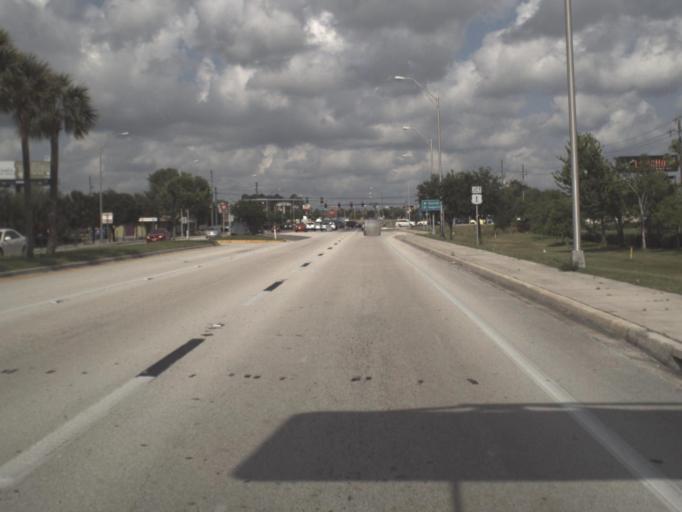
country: US
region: Florida
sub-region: Saint Johns County
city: Saint Augustine South
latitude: 29.8670
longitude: -81.3206
